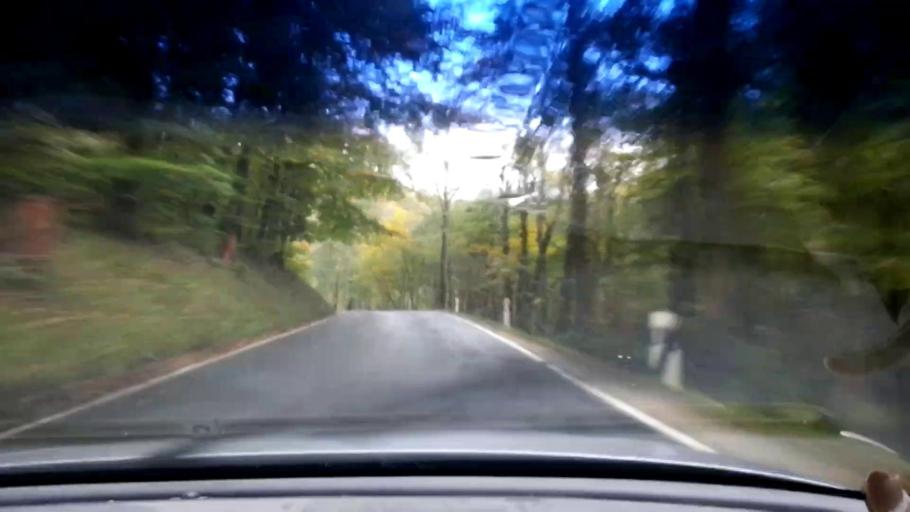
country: DE
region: Bavaria
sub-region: Upper Franconia
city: Stadelhofen
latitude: 50.0301
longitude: 11.2020
